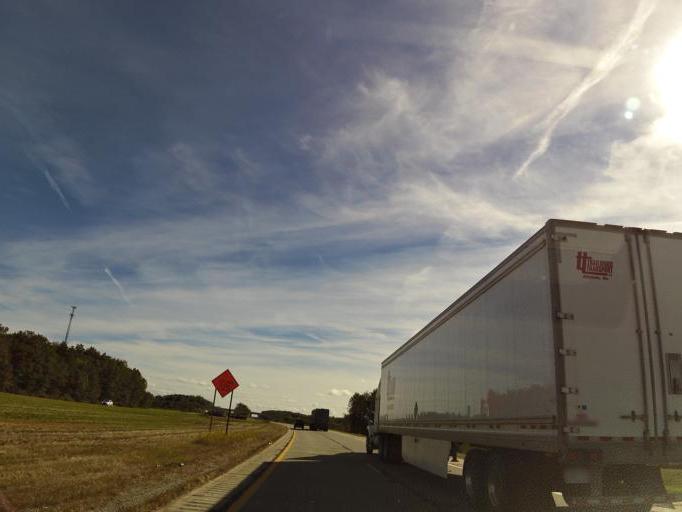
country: US
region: Michigan
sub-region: Macomb County
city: Memphis
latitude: 42.9764
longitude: -82.8310
